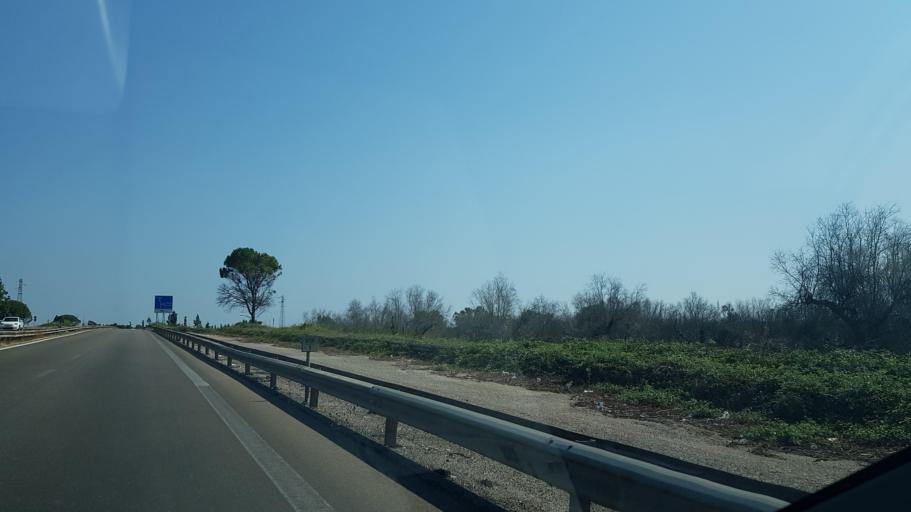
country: IT
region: Apulia
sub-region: Provincia di Lecce
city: Muro Leccese
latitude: 40.1079
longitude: 18.3186
